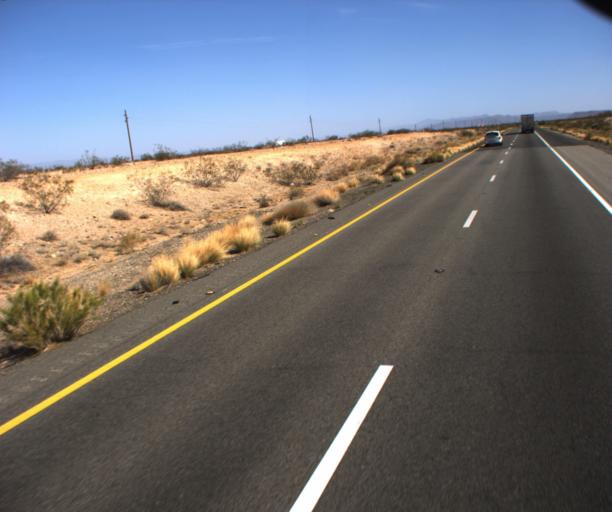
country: US
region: Arizona
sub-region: Mohave County
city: Kingman
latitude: 34.9769
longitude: -114.1407
